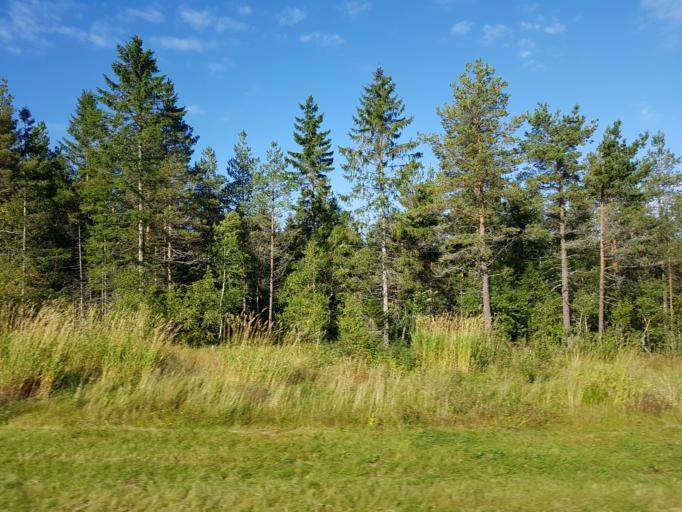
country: NO
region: Sor-Trondelag
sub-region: Trondheim
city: Trondheim
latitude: 63.5972
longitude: 10.2189
